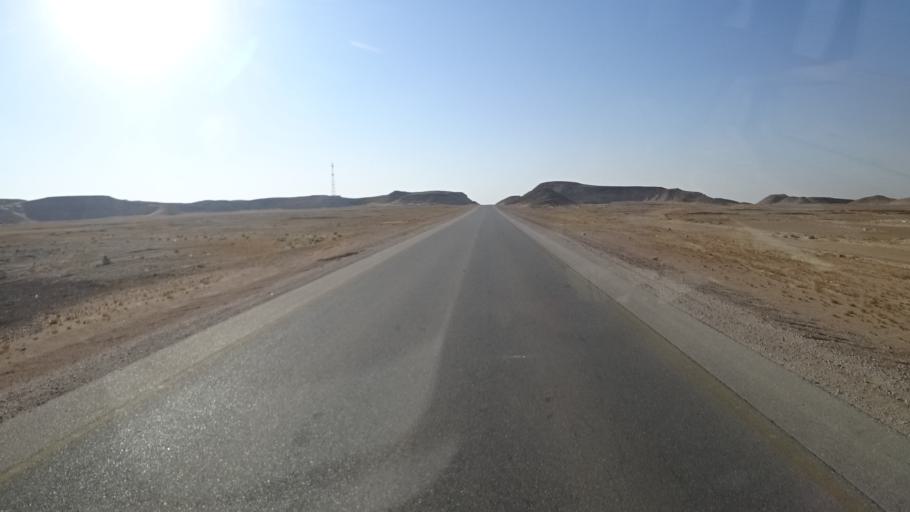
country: OM
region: Zufar
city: Salalah
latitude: 17.6413
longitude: 53.8604
